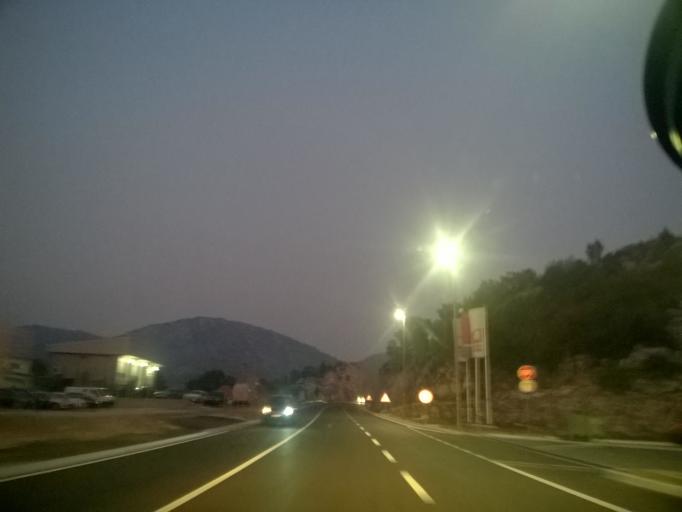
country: ME
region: Cetinje
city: Cetinje
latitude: 42.3878
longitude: 18.9338
